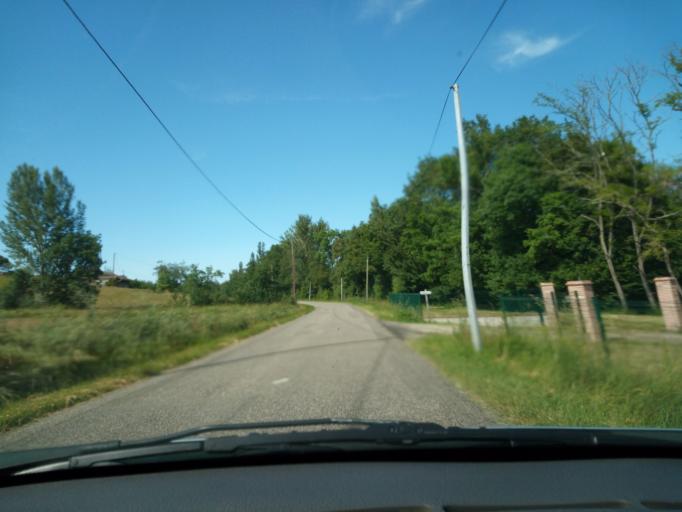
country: FR
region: Midi-Pyrenees
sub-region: Departement du Tarn-et-Garonne
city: Molieres
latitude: 44.2226
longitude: 1.3278
